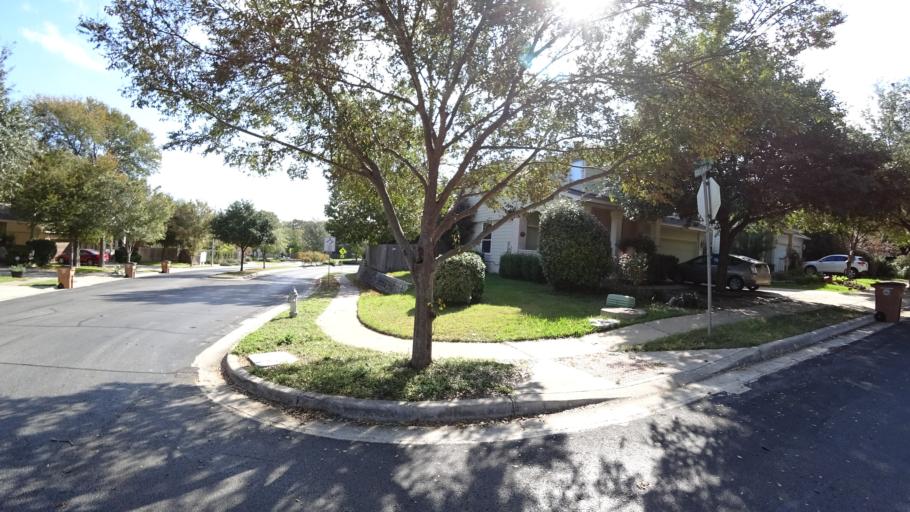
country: US
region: Texas
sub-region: Travis County
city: Shady Hollow
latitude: 30.1891
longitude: -97.8192
